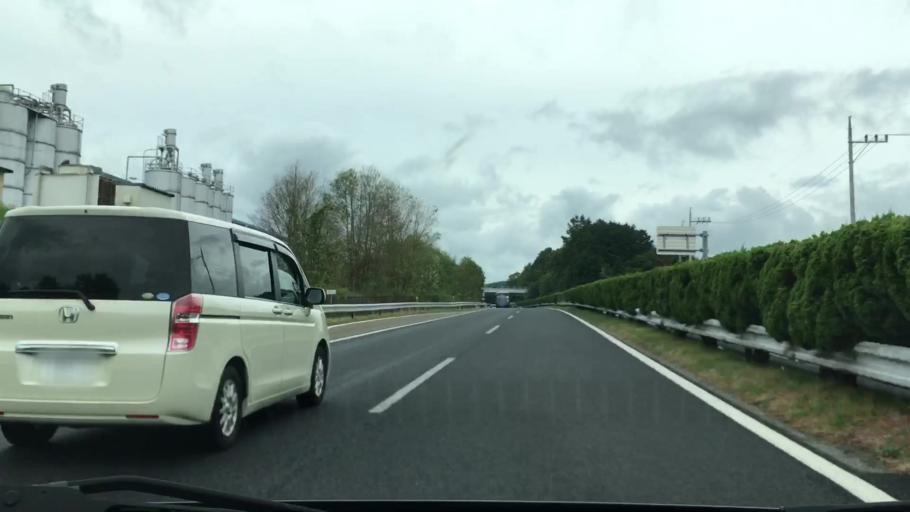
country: JP
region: Okayama
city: Tsuyama
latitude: 35.0298
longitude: 134.1557
